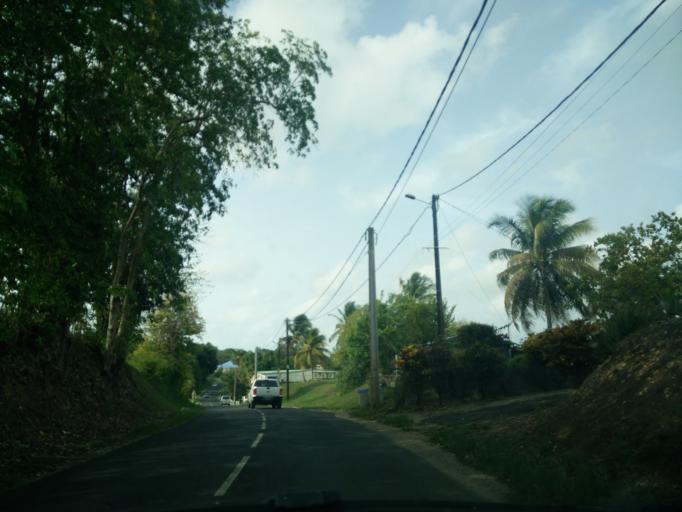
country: GP
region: Guadeloupe
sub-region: Guadeloupe
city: Le Moule
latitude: 16.3002
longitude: -61.3675
